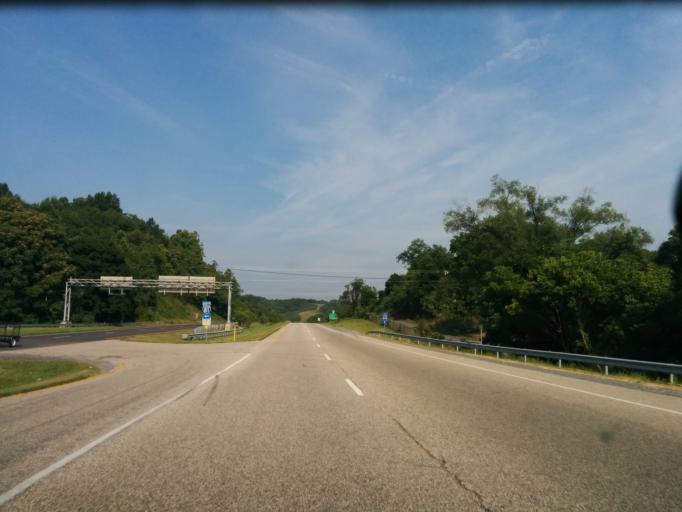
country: US
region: Virginia
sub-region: Rockbridge County
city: East Lexington
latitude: 37.7574
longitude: -79.4118
